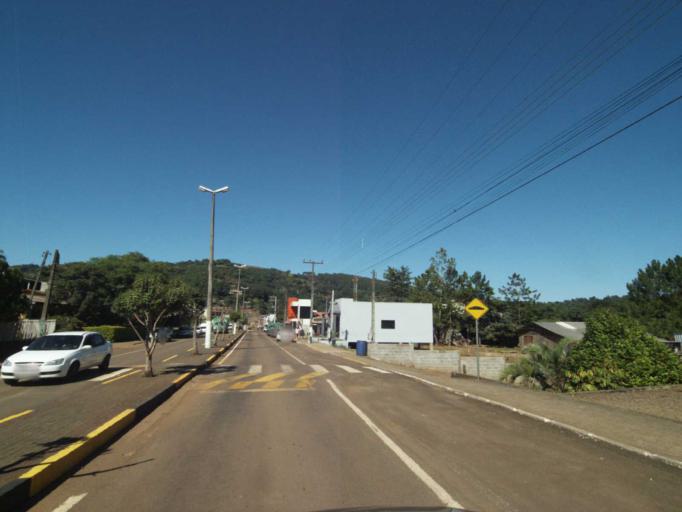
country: BR
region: Parana
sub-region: Francisco Beltrao
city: Francisco Beltrao
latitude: -26.1434
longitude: -53.3105
